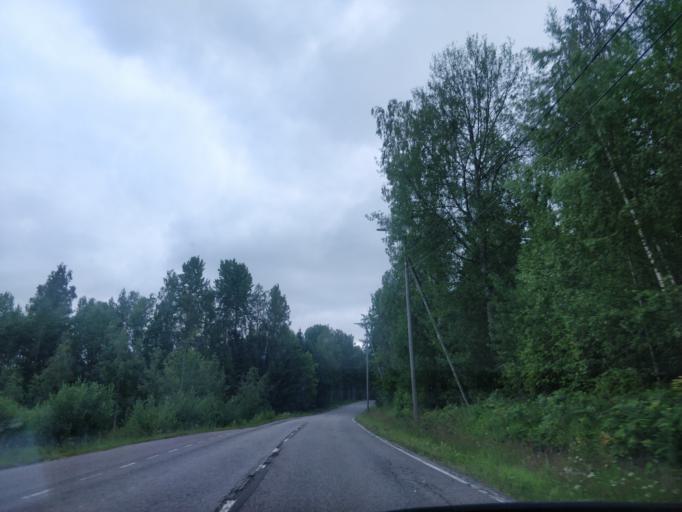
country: FI
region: Uusimaa
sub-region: Helsinki
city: Kauniainen
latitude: 60.2714
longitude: 24.7101
